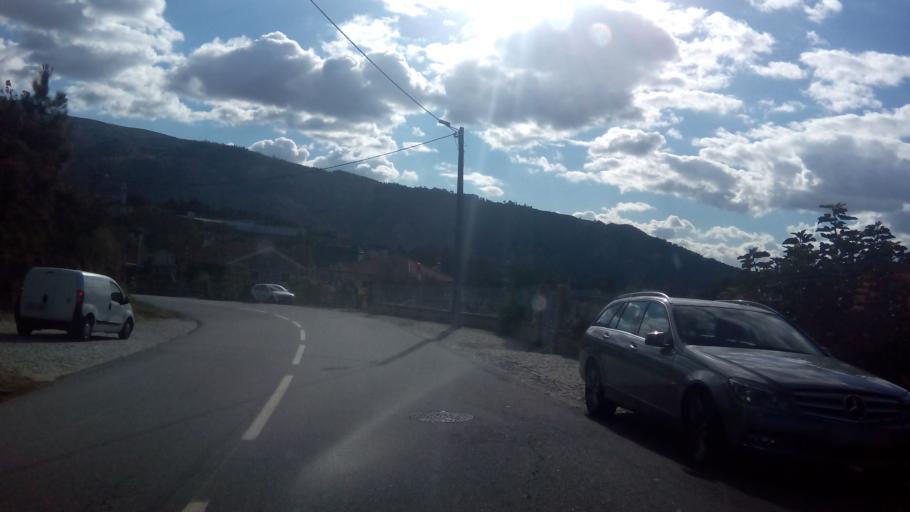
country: PT
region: Porto
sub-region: Amarante
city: Amarante
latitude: 41.2592
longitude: -8.0279
